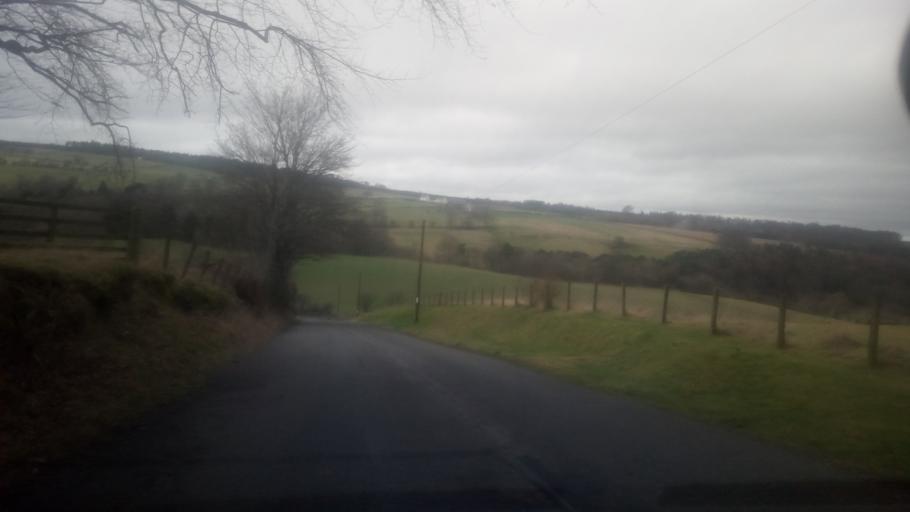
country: GB
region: Scotland
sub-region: The Scottish Borders
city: Jedburgh
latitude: 55.4865
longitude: -2.5388
